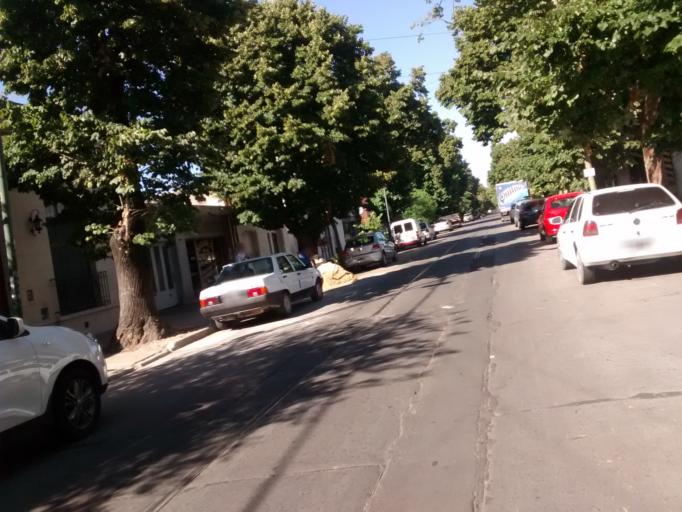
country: AR
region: Buenos Aires
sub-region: Partido de La Plata
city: La Plata
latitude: -34.9250
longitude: -57.9254
